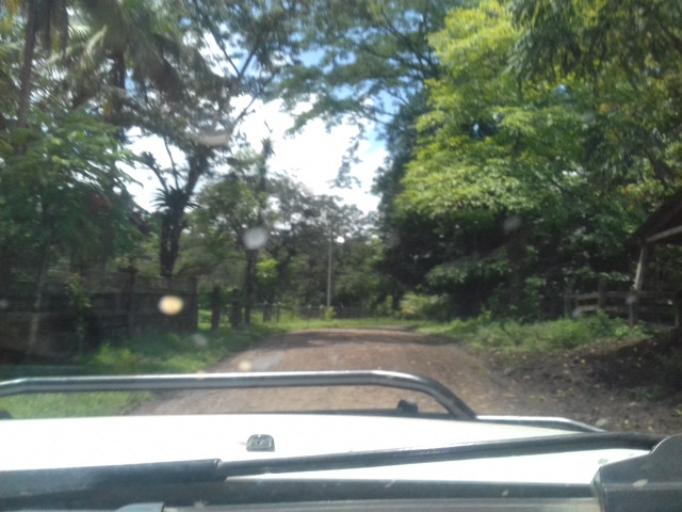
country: NI
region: Matagalpa
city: Rio Blanco
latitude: 12.9783
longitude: -85.3626
